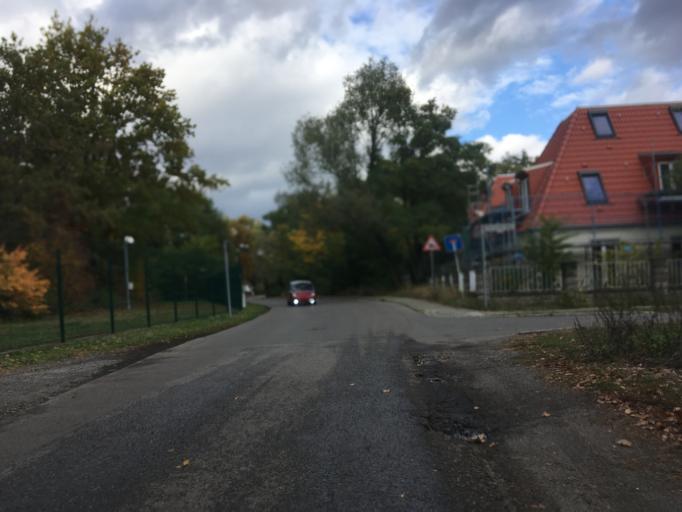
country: DE
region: Berlin
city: Adlershof
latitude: 52.4502
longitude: 13.5544
